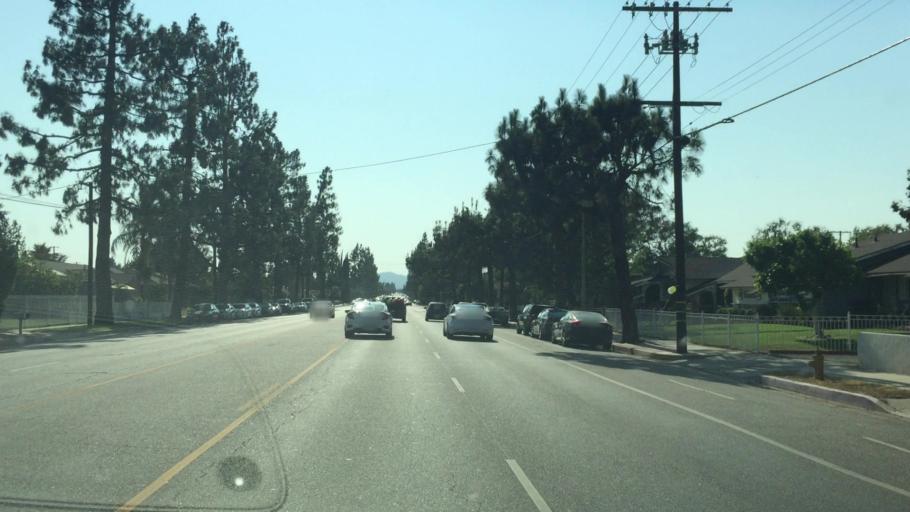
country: US
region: California
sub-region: Los Angeles County
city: San Fernando
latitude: 34.2576
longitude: -118.4866
